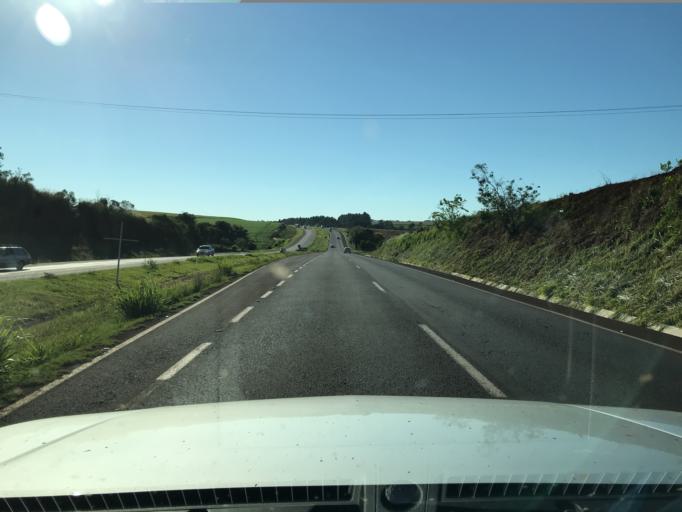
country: BR
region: Parana
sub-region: Cascavel
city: Cascavel
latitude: -24.8626
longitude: -53.5837
